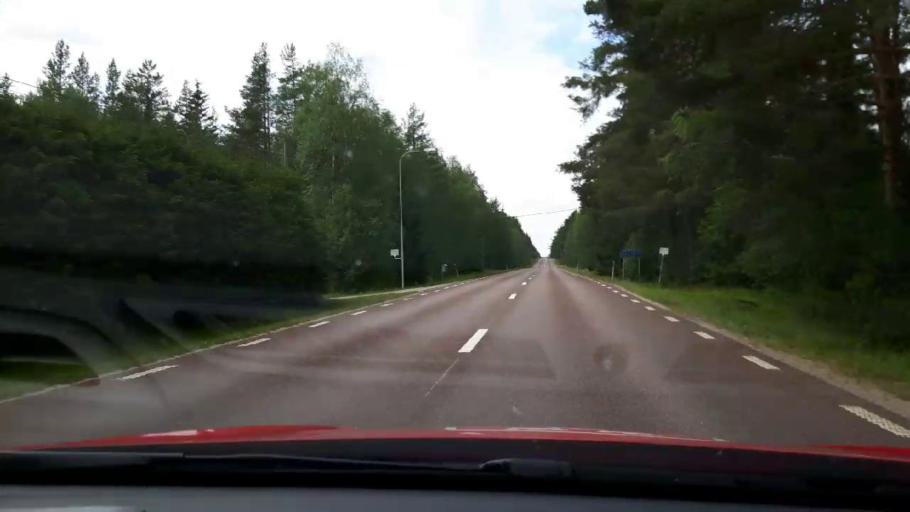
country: SE
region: Jaemtland
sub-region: Harjedalens Kommun
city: Sveg
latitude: 62.0505
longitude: 14.5089
